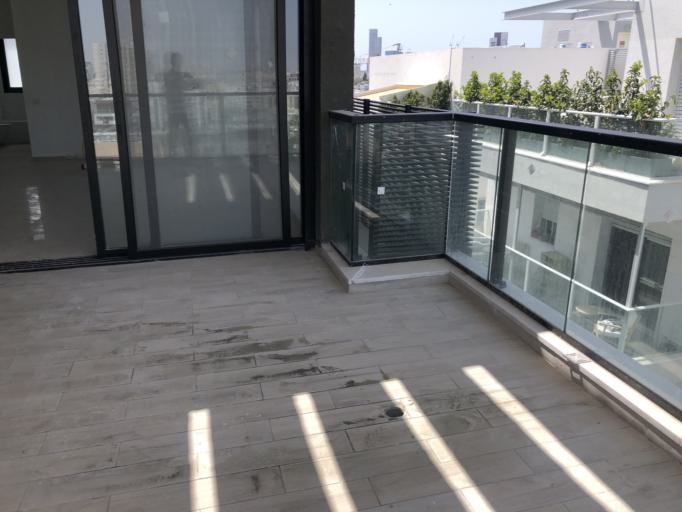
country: IL
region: Tel Aviv
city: Bene Beraq
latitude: 32.0759
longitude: 34.8274
